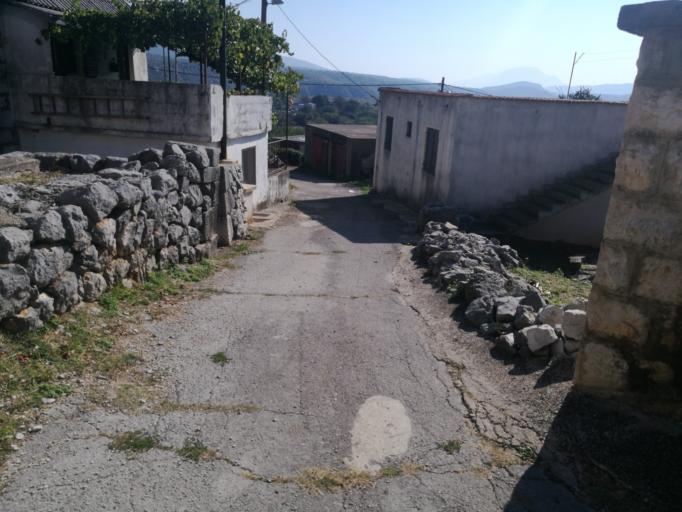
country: HR
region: Splitsko-Dalmatinska
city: Trilj
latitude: 43.5393
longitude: 16.7296
